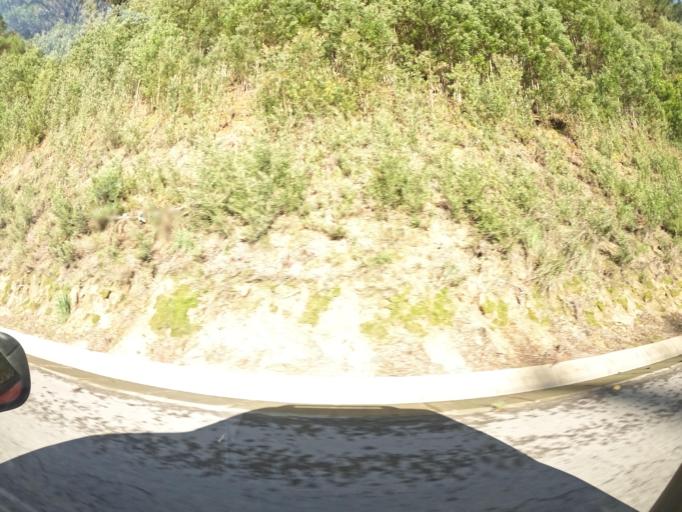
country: CL
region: Biobio
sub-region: Provincia de Concepcion
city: Chiguayante
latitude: -36.8514
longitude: -72.9146
